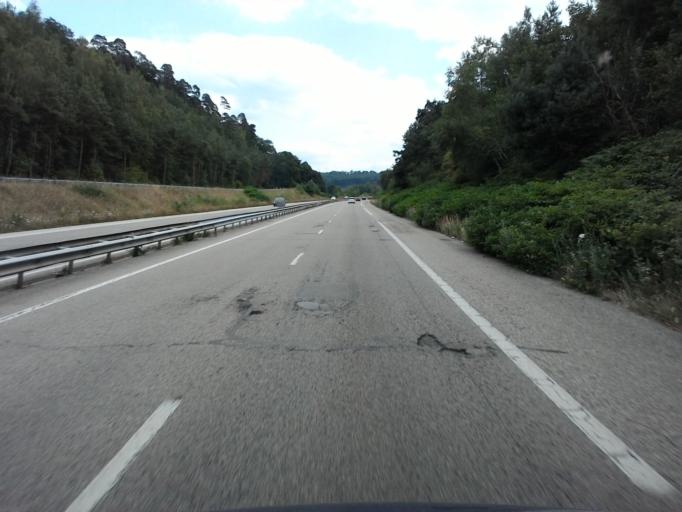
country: FR
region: Lorraine
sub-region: Departement des Vosges
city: Arches
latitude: 48.1357
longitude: 6.5150
